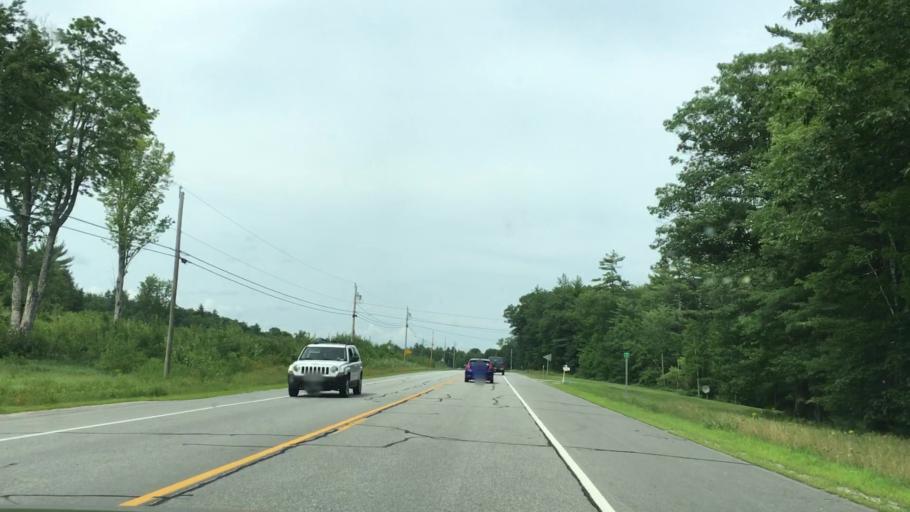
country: US
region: New Hampshire
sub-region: Hillsborough County
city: Hillsborough
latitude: 43.0980
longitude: -71.9190
